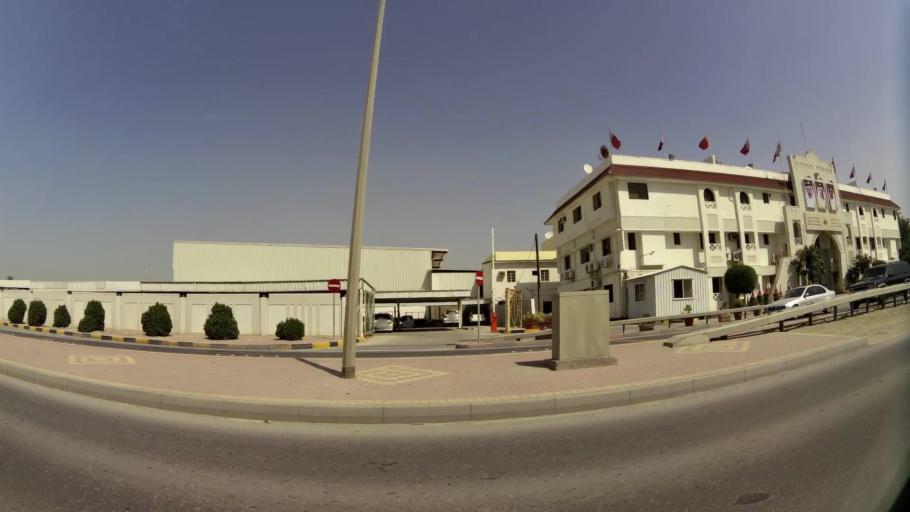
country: BH
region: Manama
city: Jidd Hafs
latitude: 26.1999
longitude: 50.4601
